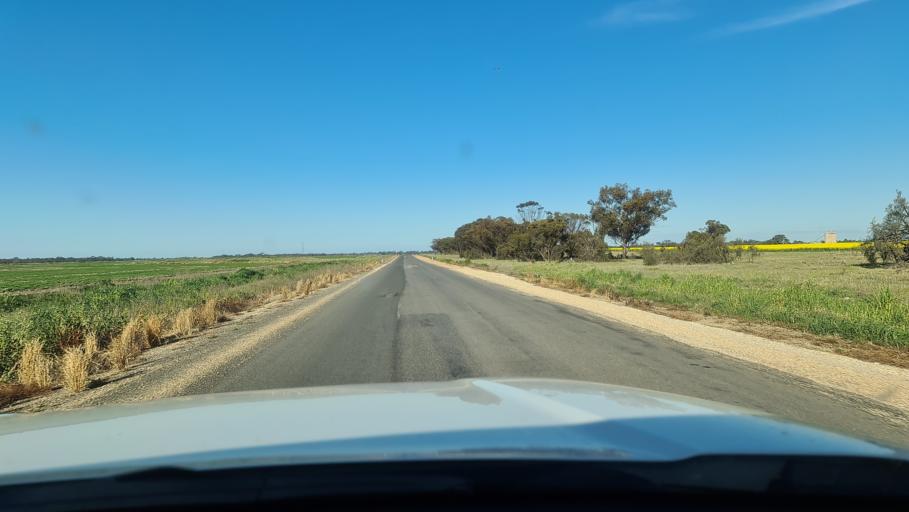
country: AU
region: Victoria
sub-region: Horsham
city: Horsham
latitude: -36.4492
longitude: 142.5639
